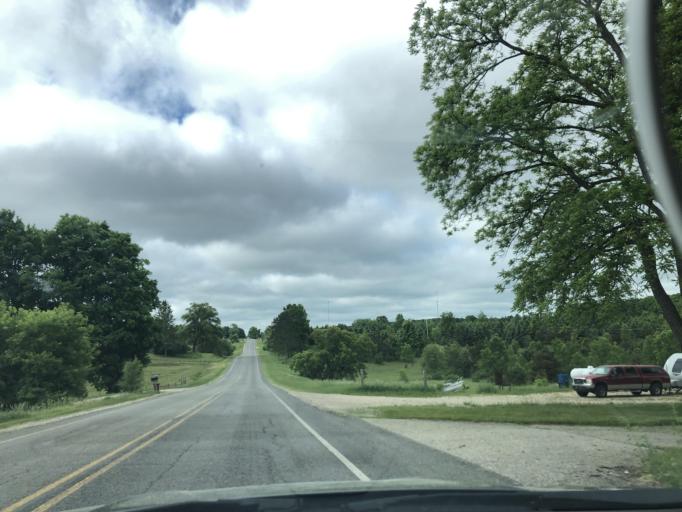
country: US
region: Michigan
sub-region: Missaukee County
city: Lake City
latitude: 44.4455
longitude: -85.2165
